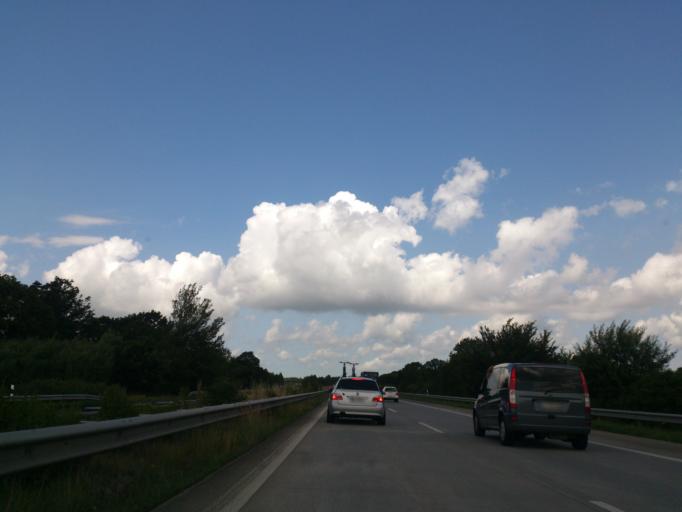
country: DE
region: Schleswig-Holstein
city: Dageling
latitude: 53.8830
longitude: 9.5453
